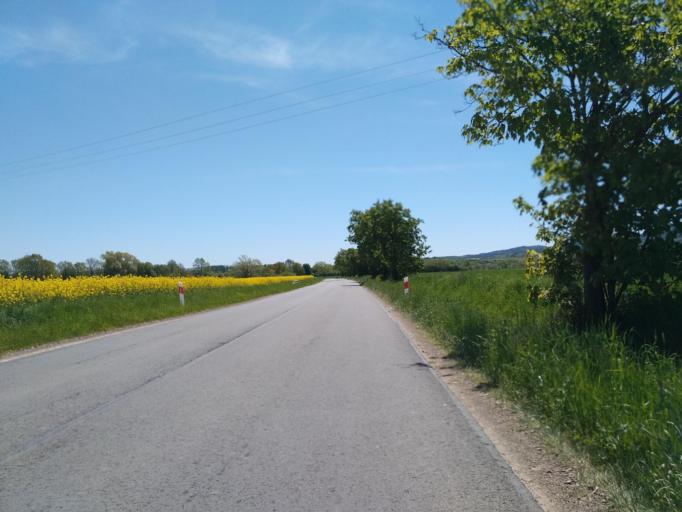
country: PL
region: Subcarpathian Voivodeship
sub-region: Powiat krosnienski
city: Sieniawa
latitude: 49.5477
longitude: 21.9451
